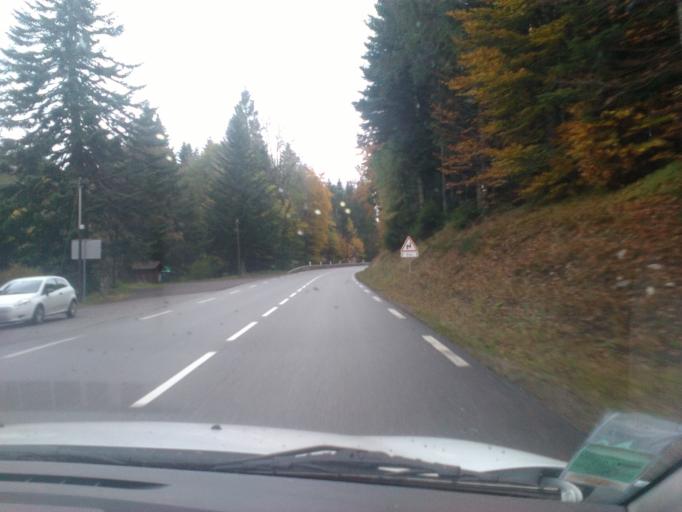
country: FR
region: Lorraine
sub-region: Departement des Vosges
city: Xonrupt-Longemer
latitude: 48.1018
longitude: 6.9056
